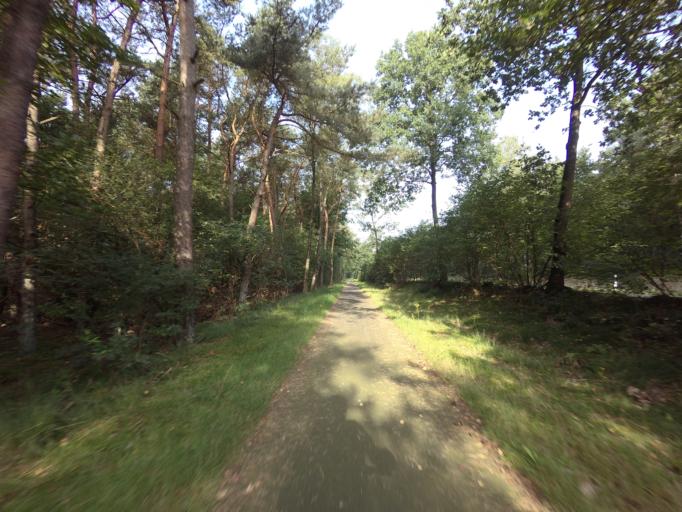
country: DE
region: Lower Saxony
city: Wielen
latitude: 52.5217
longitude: 6.7468
